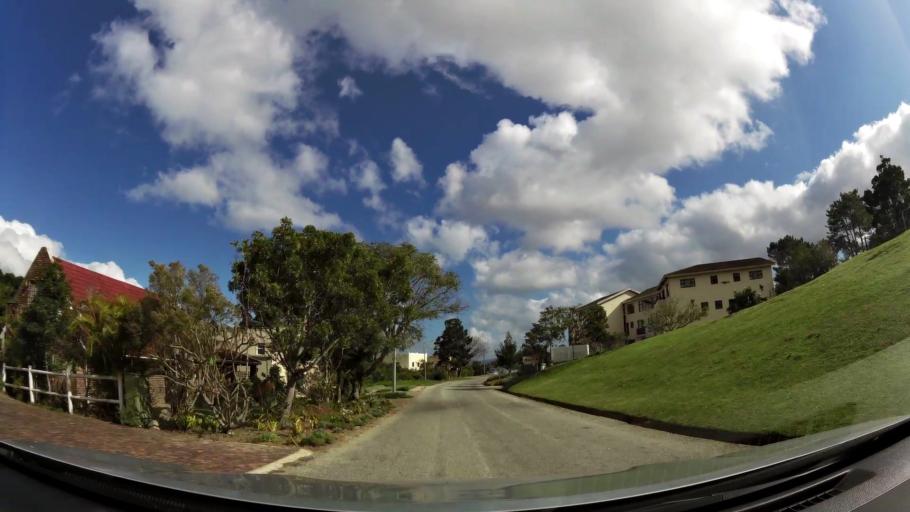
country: ZA
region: Western Cape
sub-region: Eden District Municipality
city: Knysna
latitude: -34.0522
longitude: 23.0814
